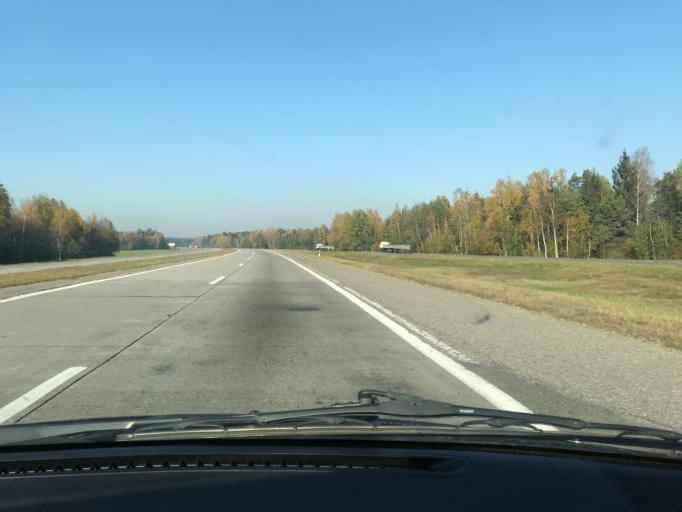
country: BY
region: Minsk
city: Uzda
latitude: 53.3702
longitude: 27.5055
